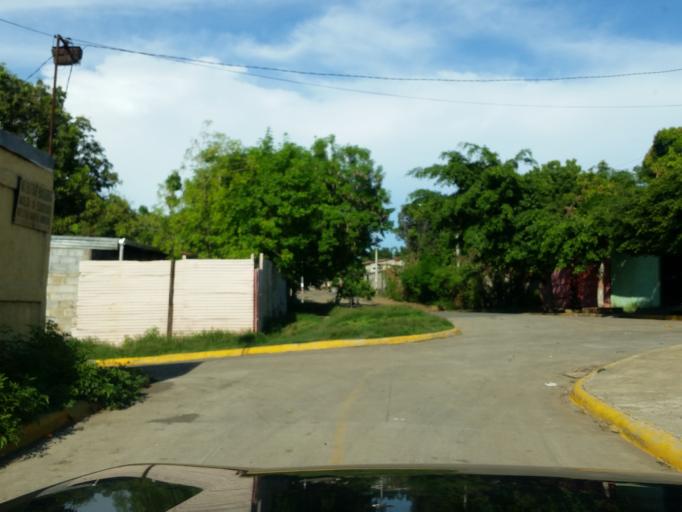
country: NI
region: Managua
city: Managua
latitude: 12.1080
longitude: -86.2255
